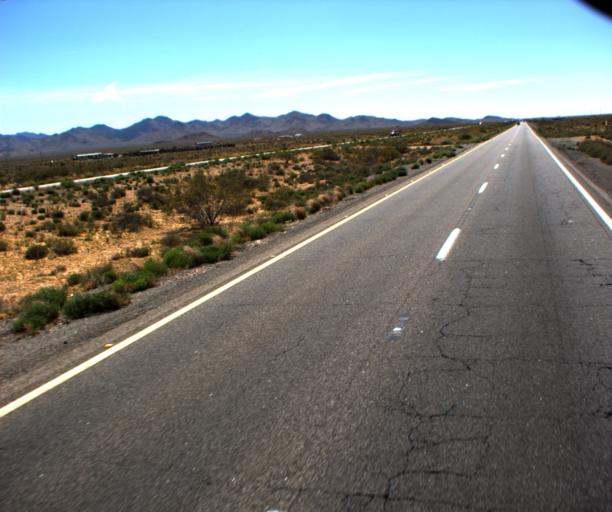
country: US
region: Arizona
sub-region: Mohave County
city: Dolan Springs
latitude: 35.5010
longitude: -114.3329
